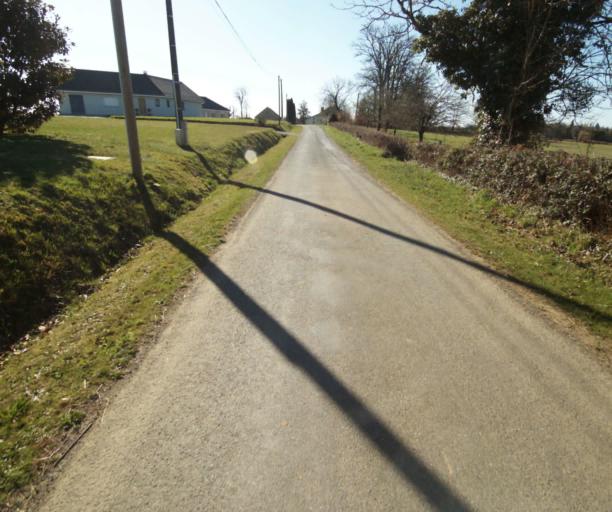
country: FR
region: Limousin
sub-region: Departement de la Correze
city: Seilhac
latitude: 45.3893
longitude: 1.7547
